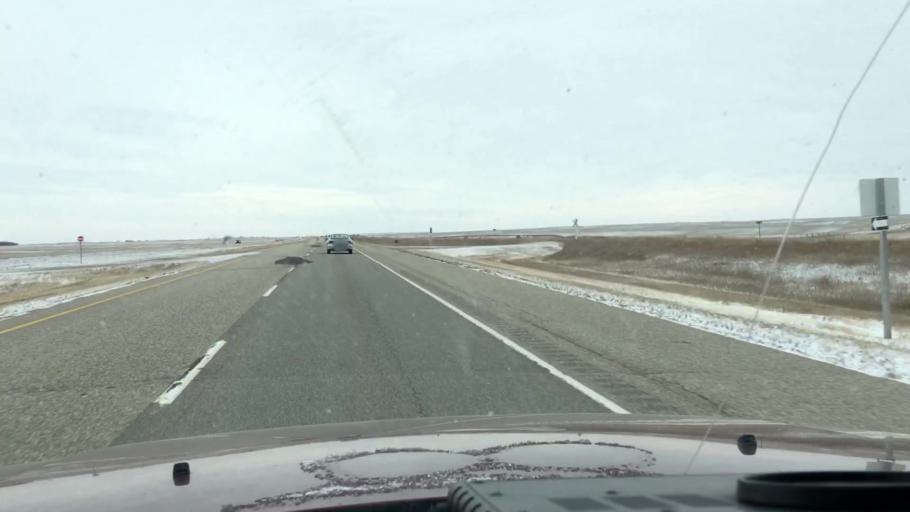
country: CA
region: Saskatchewan
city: Saskatoon
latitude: 51.4644
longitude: -106.2391
